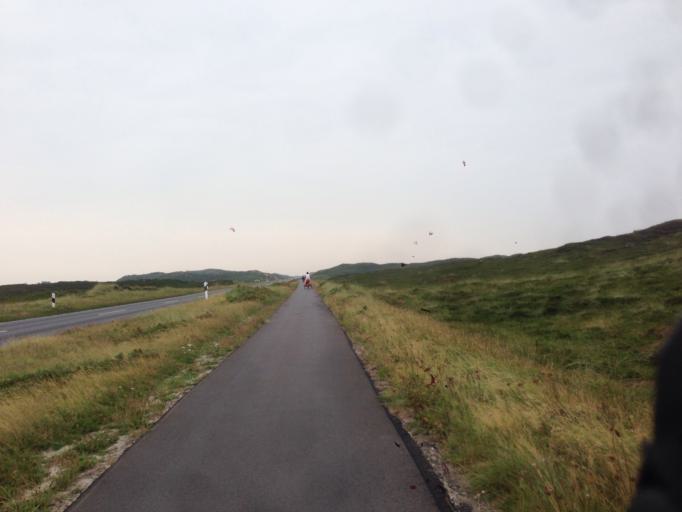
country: DE
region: Schleswig-Holstein
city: Westerland
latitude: 54.8079
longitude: 8.2881
